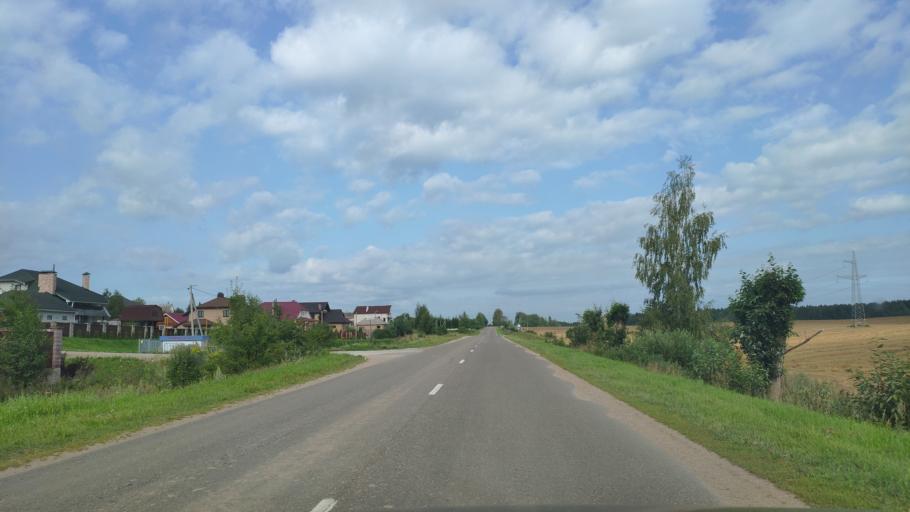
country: BY
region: Minsk
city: Khatsyezhyna
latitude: 53.8708
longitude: 27.3112
